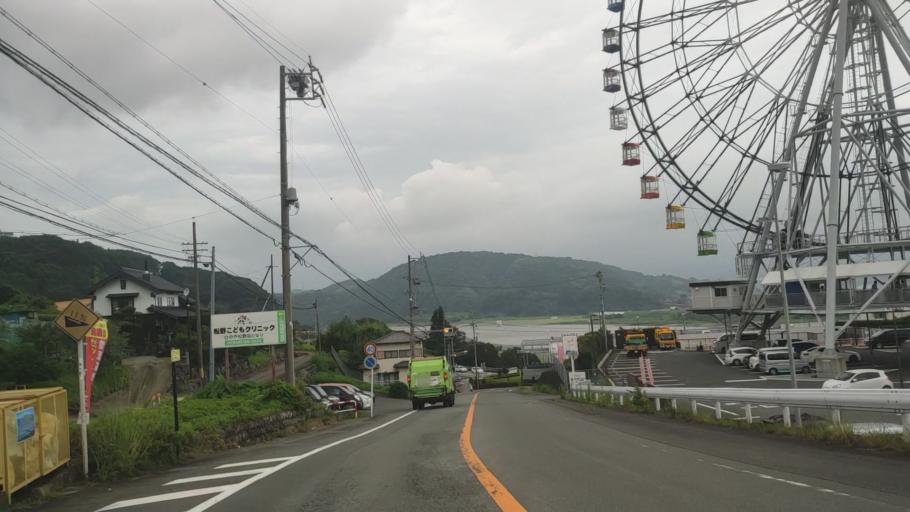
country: JP
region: Shizuoka
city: Fujinomiya
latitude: 35.1617
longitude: 138.6167
